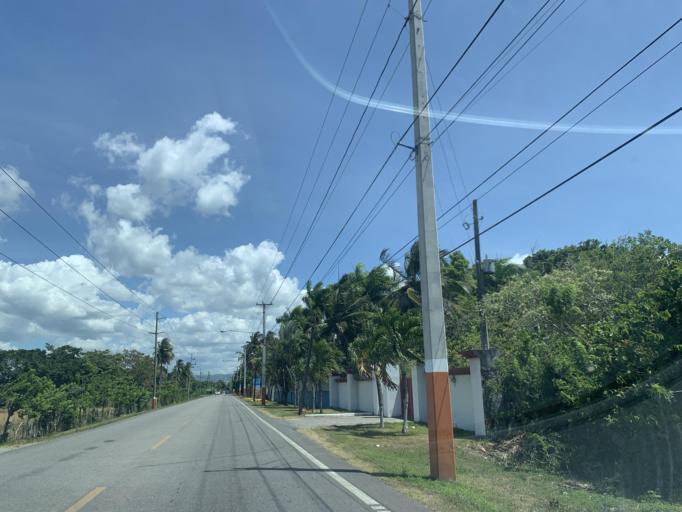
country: DO
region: Puerto Plata
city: Cabarete
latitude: 19.7147
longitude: -70.3855
